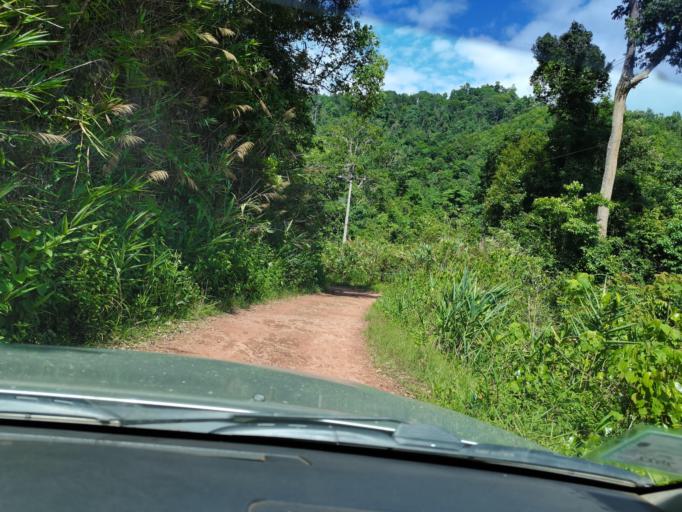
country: LA
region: Loungnamtha
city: Muang Nale
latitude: 20.5448
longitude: 101.0640
